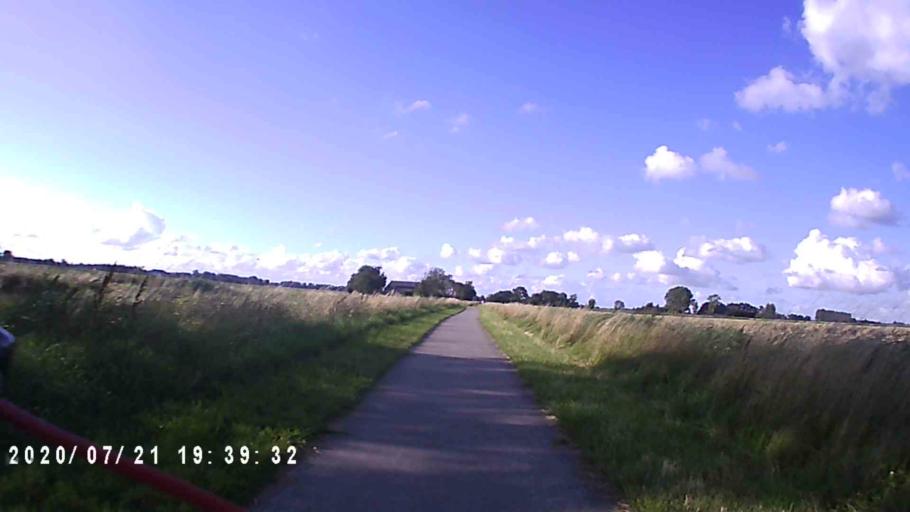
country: NL
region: Groningen
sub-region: Gemeente Groningen
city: Oosterpark
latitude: 53.2551
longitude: 6.6067
